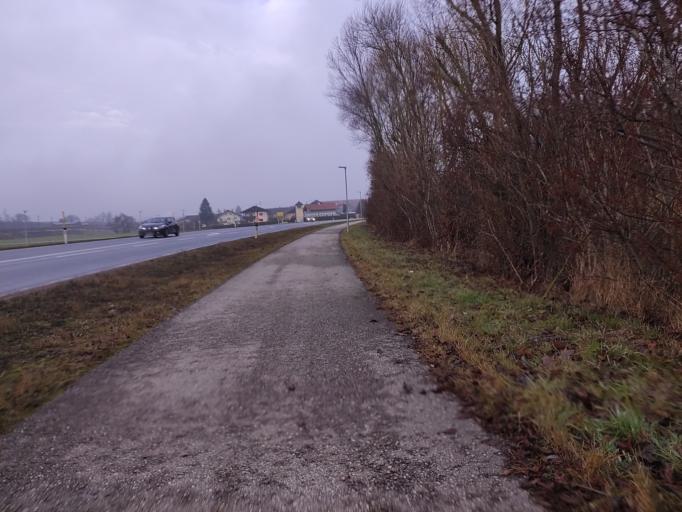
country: AT
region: Salzburg
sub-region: Politischer Bezirk Salzburg-Umgebung
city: Strasswalchen
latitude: 47.9713
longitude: 13.2716
